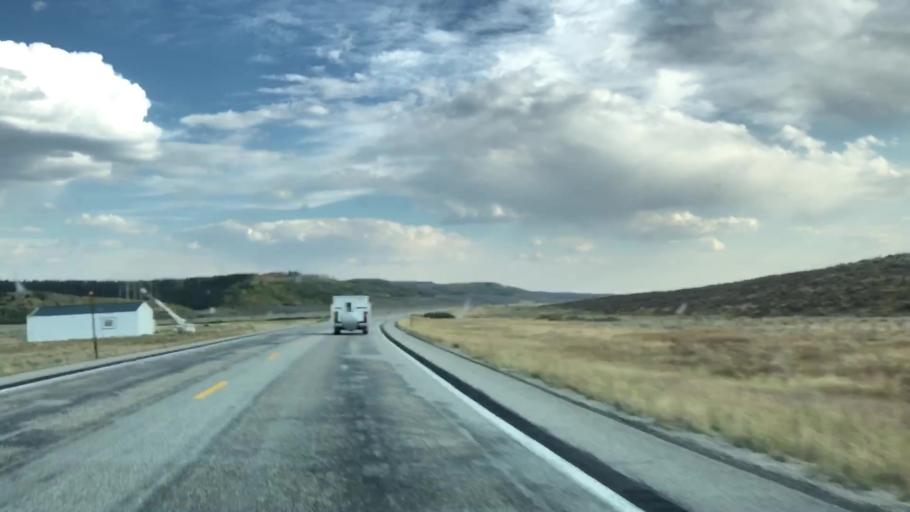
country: US
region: Wyoming
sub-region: Sublette County
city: Pinedale
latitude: 43.1163
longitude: -110.1772
